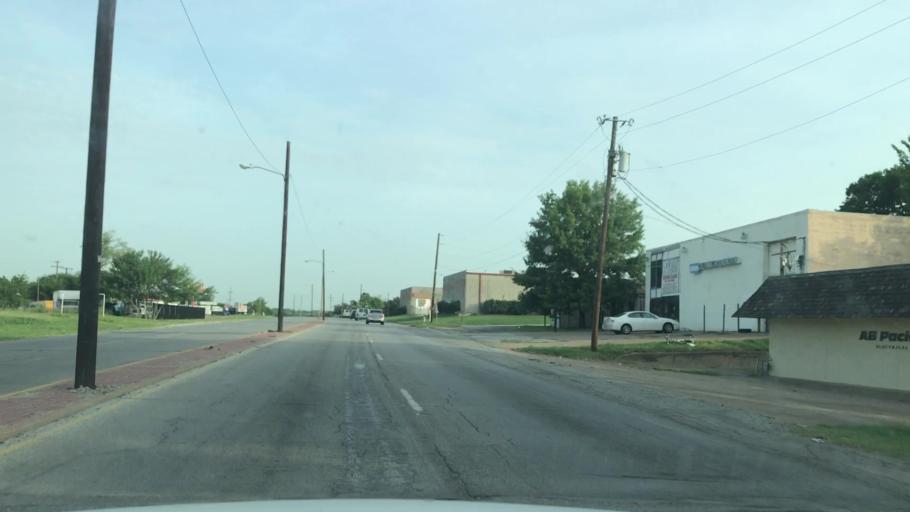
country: US
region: Texas
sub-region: Dallas County
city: Dallas
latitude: 32.7800
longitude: -96.7226
